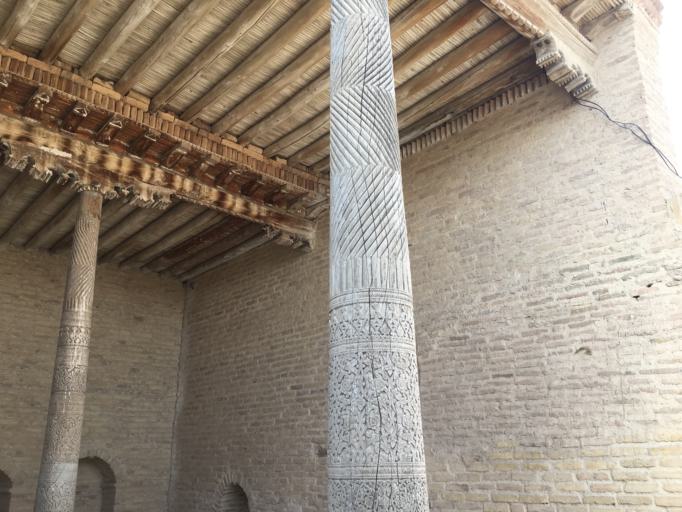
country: TM
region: Dasoguz
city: Tagta
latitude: 41.5692
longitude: 59.8108
